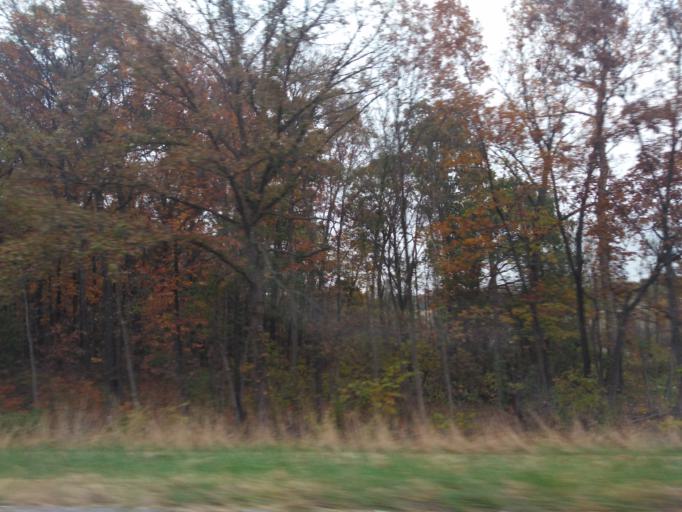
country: US
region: Illinois
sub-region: Bond County
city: Greenville
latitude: 38.8342
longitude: -89.5272
